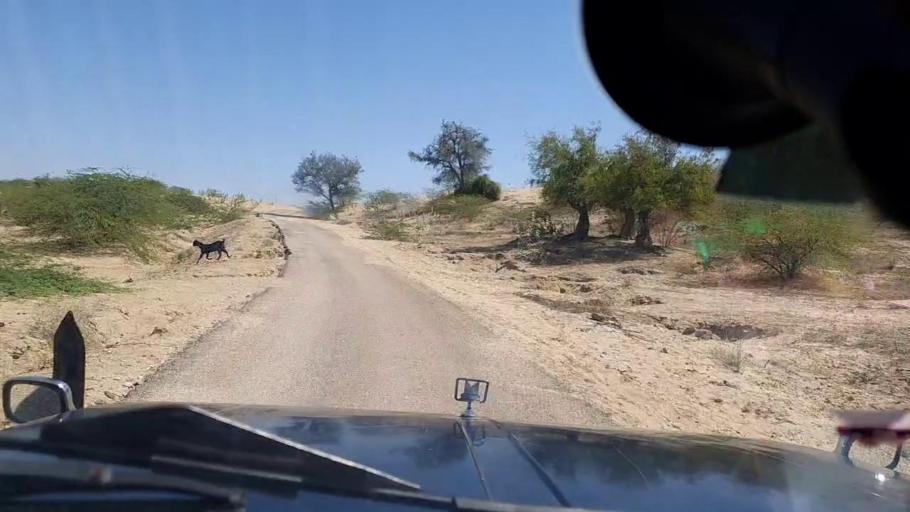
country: PK
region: Sindh
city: Diplo
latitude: 24.5613
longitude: 69.6747
